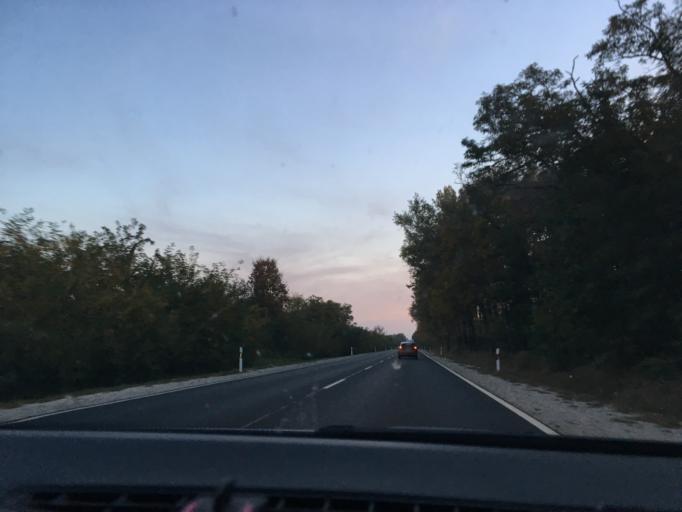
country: HU
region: Hajdu-Bihar
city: Debrecen
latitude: 47.5773
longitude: 21.6541
